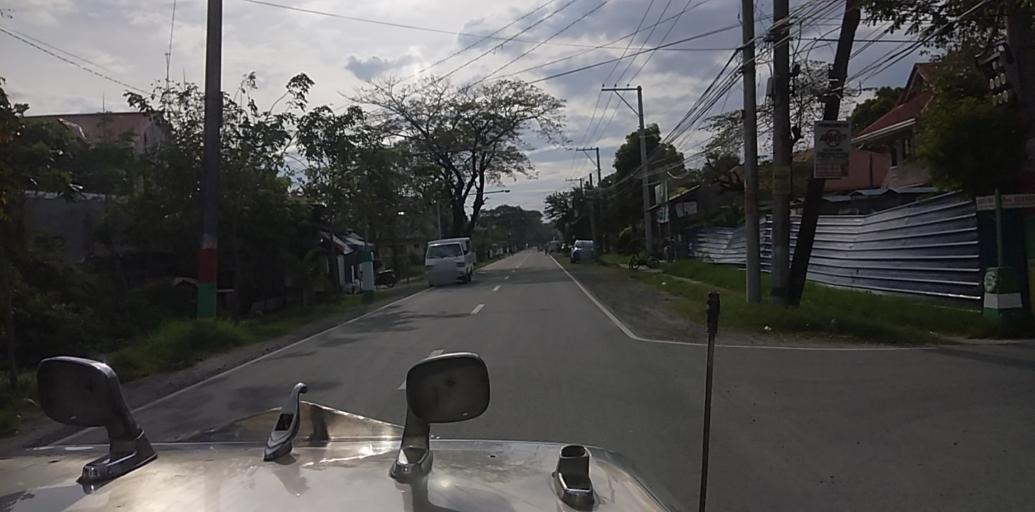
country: PH
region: Central Luzon
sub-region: Province of Pampanga
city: Minalin
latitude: 14.9780
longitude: 120.6889
